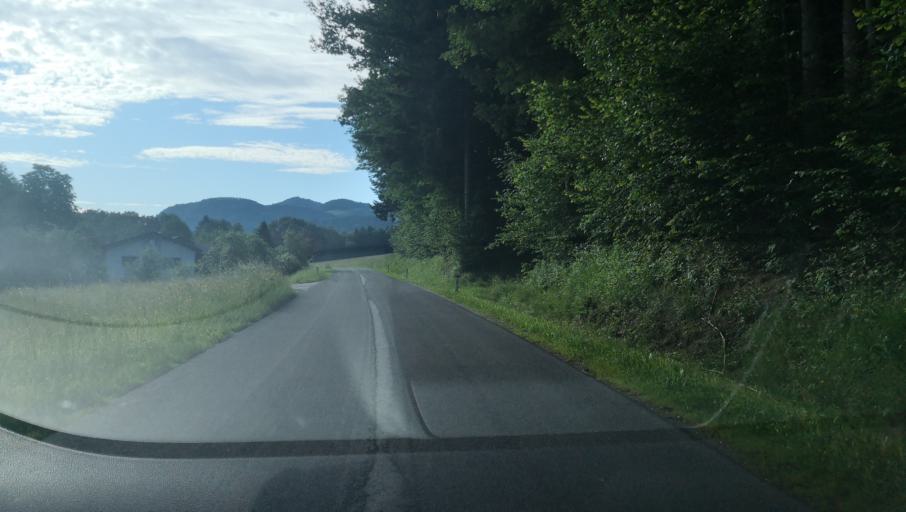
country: AT
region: Lower Austria
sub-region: Politischer Bezirk Scheibbs
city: Gresten
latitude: 48.0036
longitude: 15.0468
